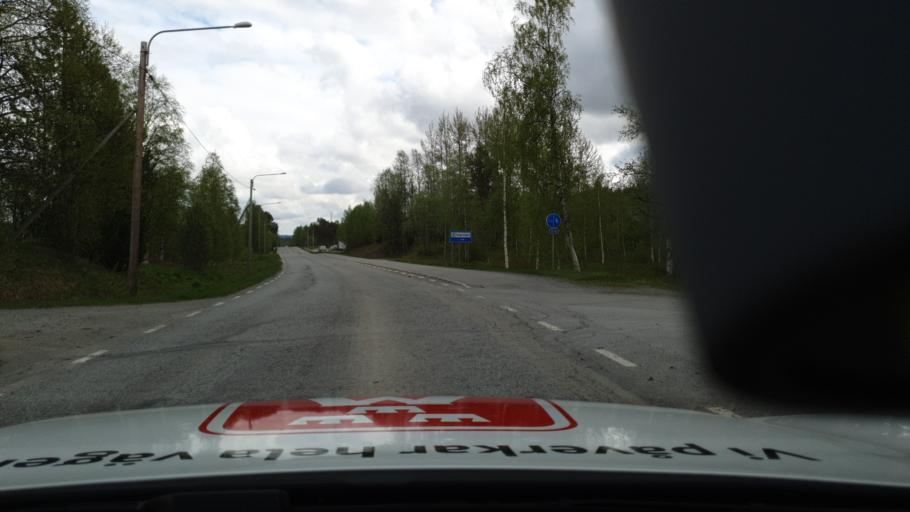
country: SE
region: Vaesterbotten
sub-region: Vilhelmina Kommun
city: Sjoberg
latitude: 64.6398
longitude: 16.3600
